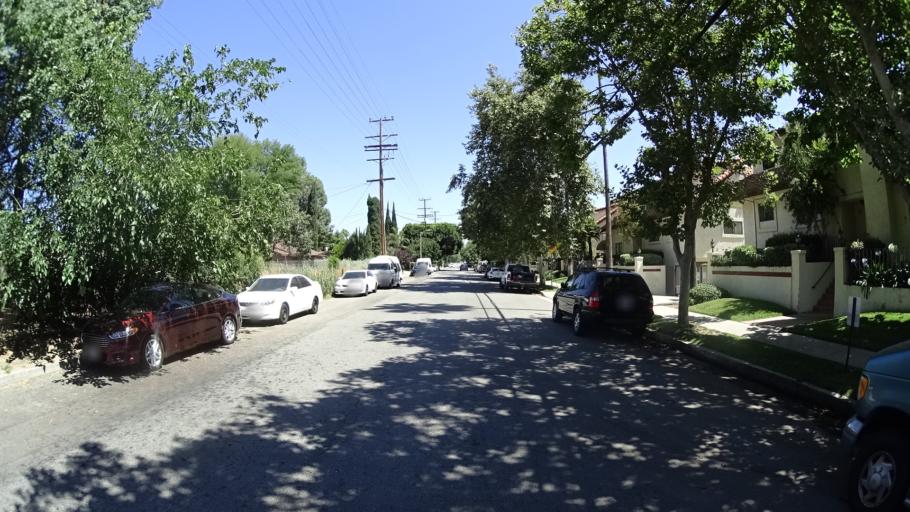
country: US
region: California
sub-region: Los Angeles County
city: Van Nuys
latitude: 34.1962
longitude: -118.4946
